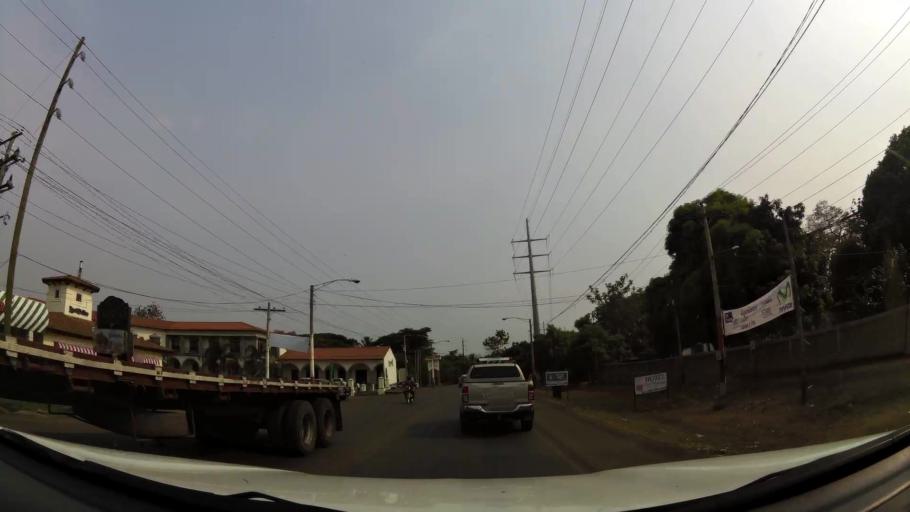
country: NI
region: Chinandega
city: Chinandega
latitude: 12.6287
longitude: -87.1185
